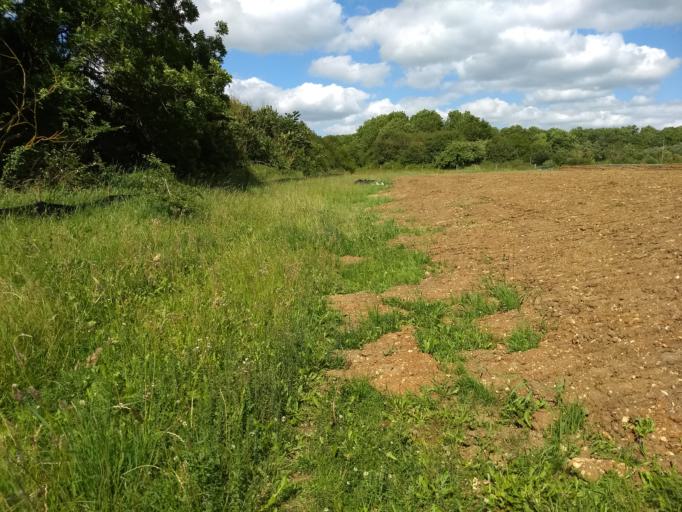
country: GB
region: England
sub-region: Milton Keynes
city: Calverton
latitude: 52.0488
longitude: -0.8414
